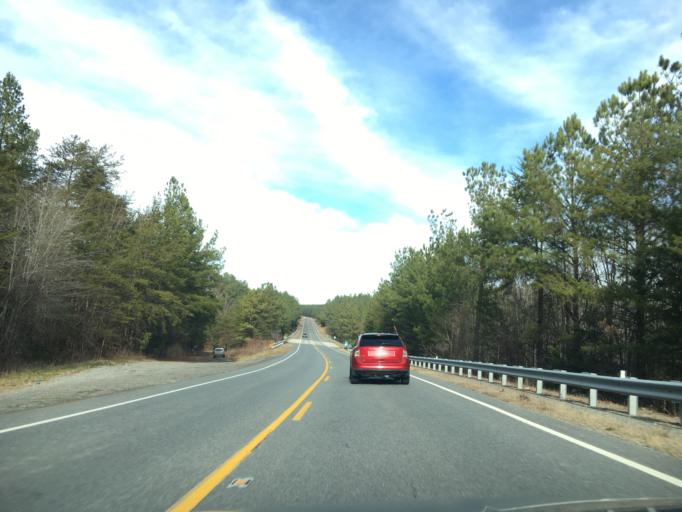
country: US
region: Virginia
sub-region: Louisa County
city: Louisa
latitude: 38.0637
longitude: -77.8793
